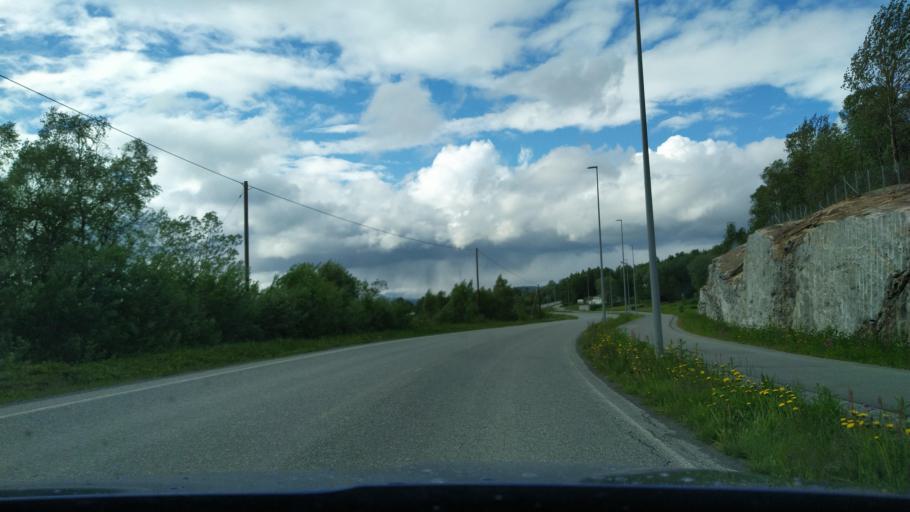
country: NO
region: Troms
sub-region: Lenvik
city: Finnsnes
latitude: 69.1797
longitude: 18.0580
